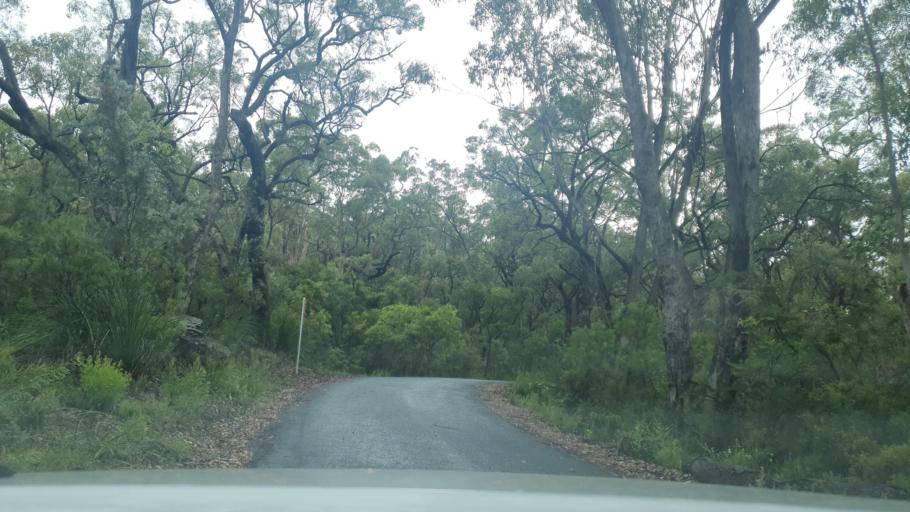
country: AU
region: New South Wales
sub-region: Blue Mountains Municipality
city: Glenbrook
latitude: -33.7802
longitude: 150.6199
